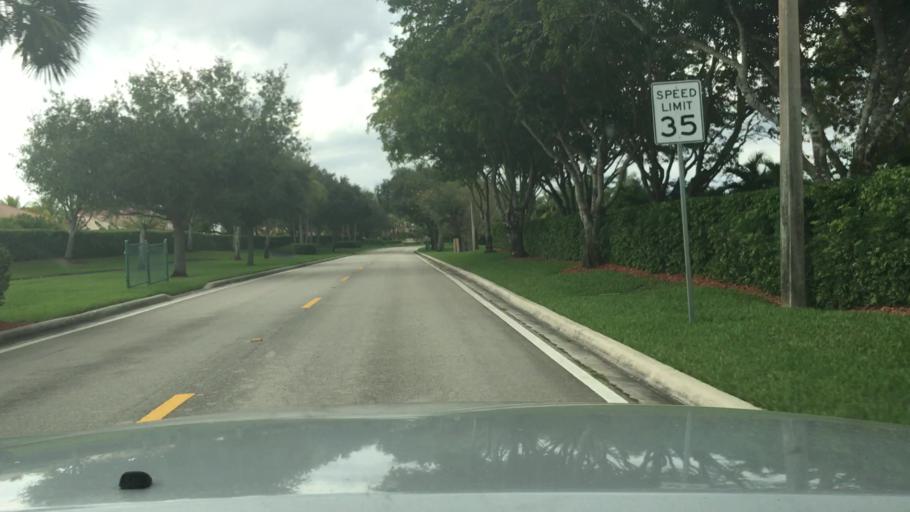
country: US
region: Florida
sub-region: Broward County
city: Sunshine Ranches
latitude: 26.0026
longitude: -80.3674
